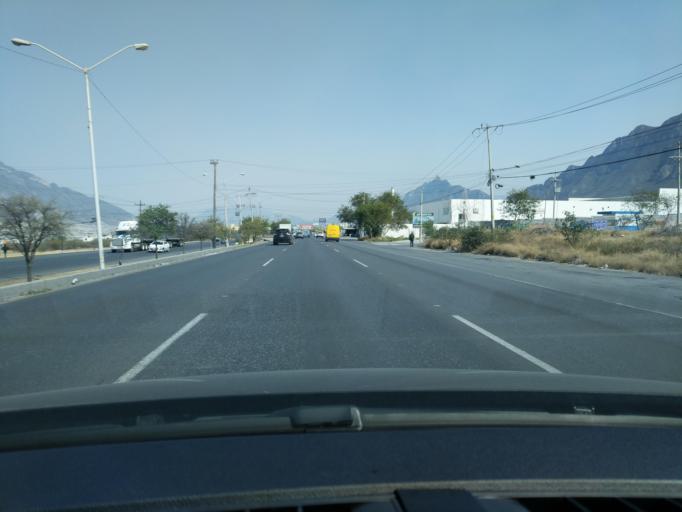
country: MX
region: Nuevo Leon
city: Santa Catarina
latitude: 25.6902
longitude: -100.5028
